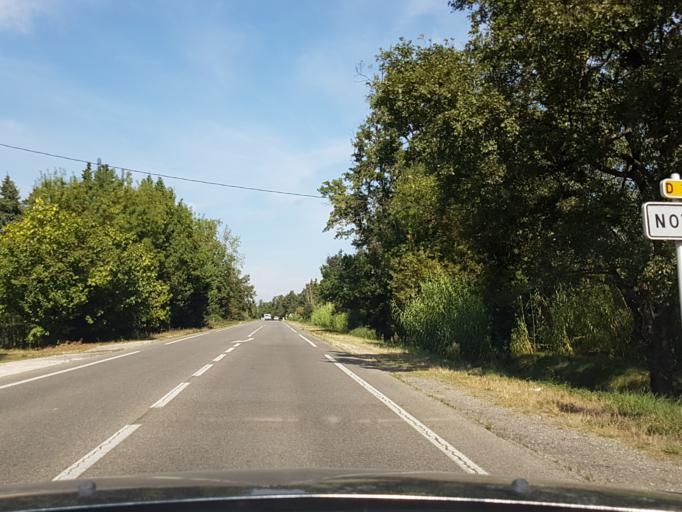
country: FR
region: Provence-Alpes-Cote d'Azur
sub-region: Departement des Bouches-du-Rhone
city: Noves
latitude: 43.8483
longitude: 4.9005
